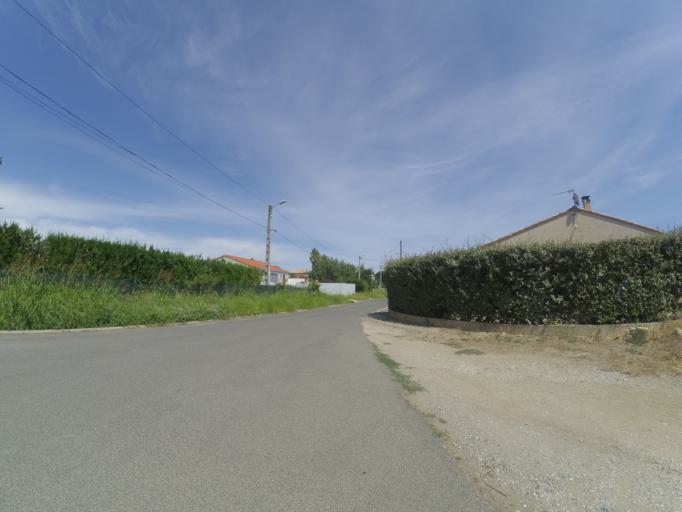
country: FR
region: Languedoc-Roussillon
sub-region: Departement des Pyrenees-Orientales
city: Millas
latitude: 42.6896
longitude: 2.6870
